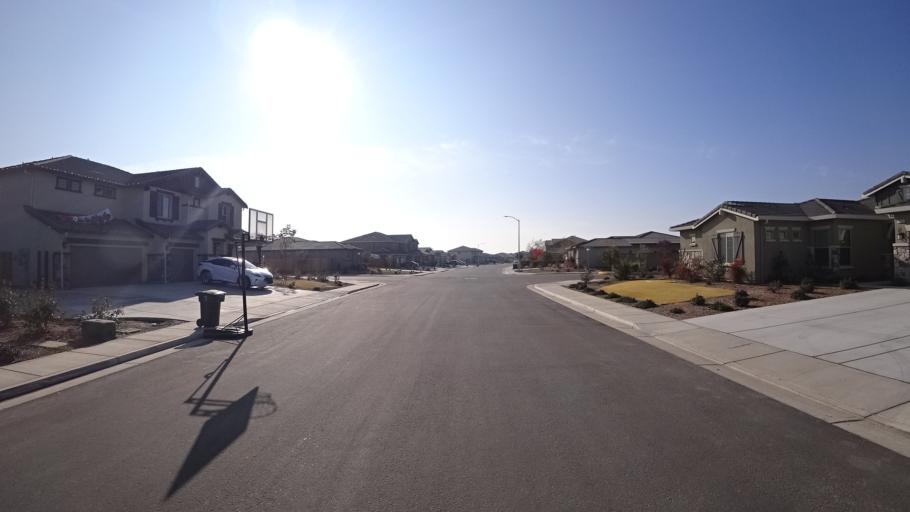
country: US
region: California
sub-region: Kern County
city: Rosedale
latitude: 35.3507
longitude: -119.1692
